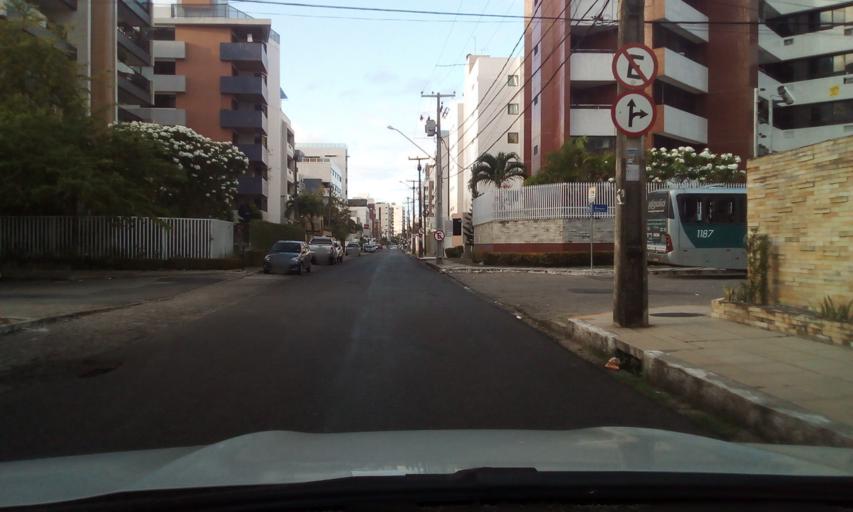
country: BR
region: Paraiba
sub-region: Joao Pessoa
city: Joao Pessoa
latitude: -7.1267
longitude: -34.8250
